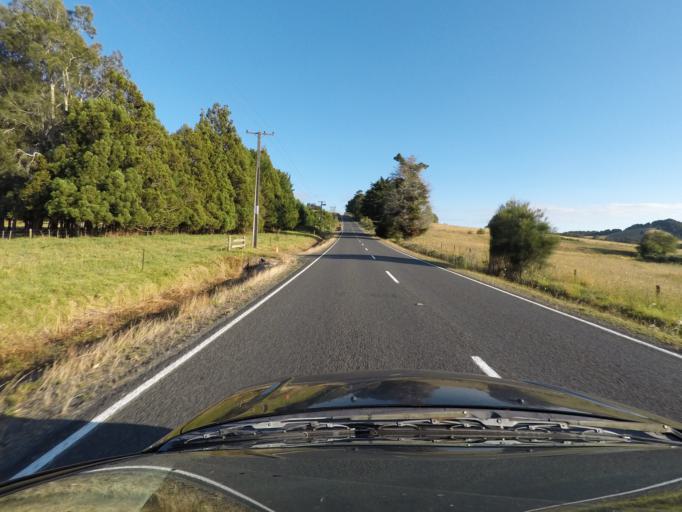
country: NZ
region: Northland
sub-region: Whangarei
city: Whangarei
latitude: -35.6743
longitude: 174.3266
